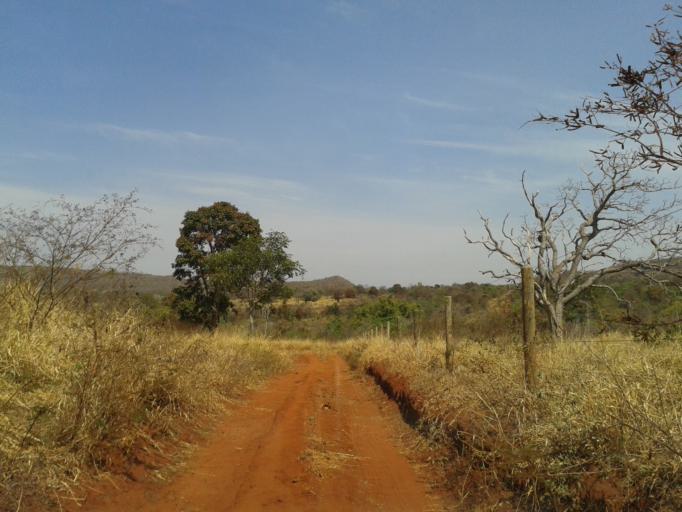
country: BR
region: Minas Gerais
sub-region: Santa Vitoria
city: Santa Vitoria
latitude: -19.2058
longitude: -50.0349
